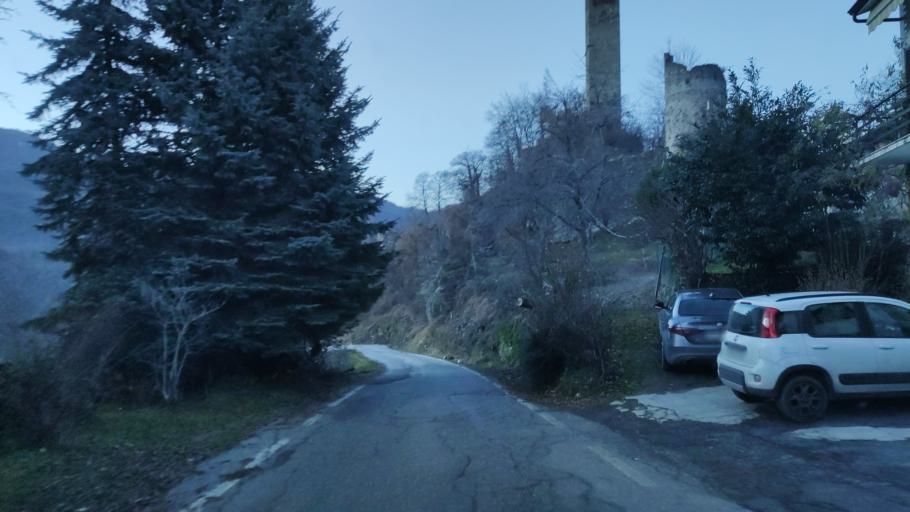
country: IT
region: Piedmont
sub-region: Provincia di Cuneo
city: Lisio
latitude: 44.2936
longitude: 7.9820
